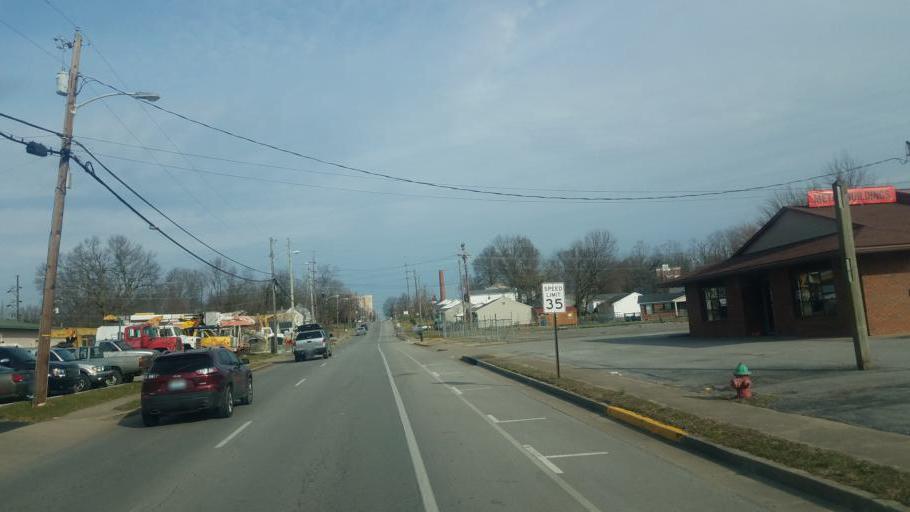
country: US
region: Kentucky
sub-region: Boyle County
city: Danville
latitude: 37.6378
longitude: -84.7732
